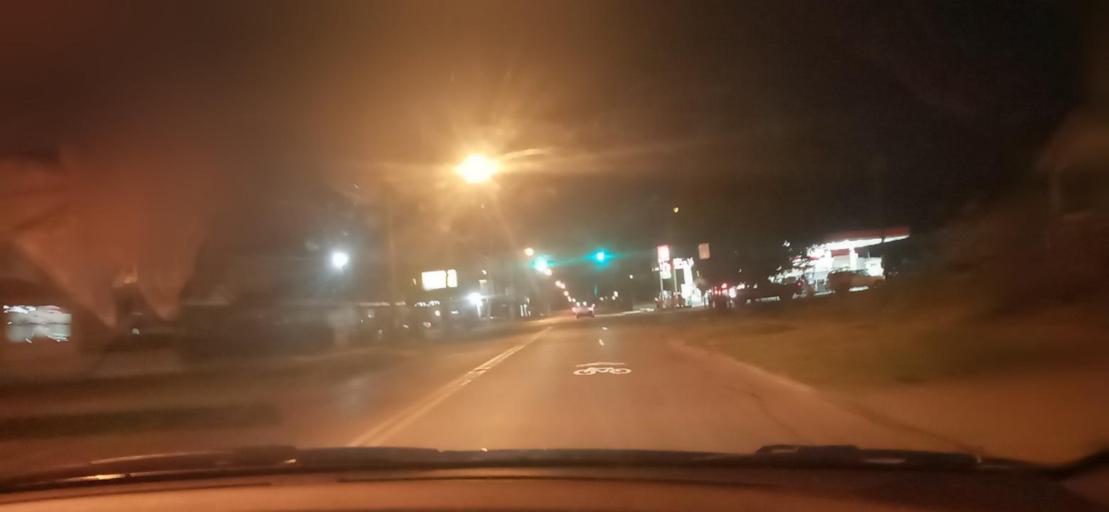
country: US
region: Ohio
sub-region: Summit County
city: Akron
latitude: 41.0538
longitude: -81.5099
